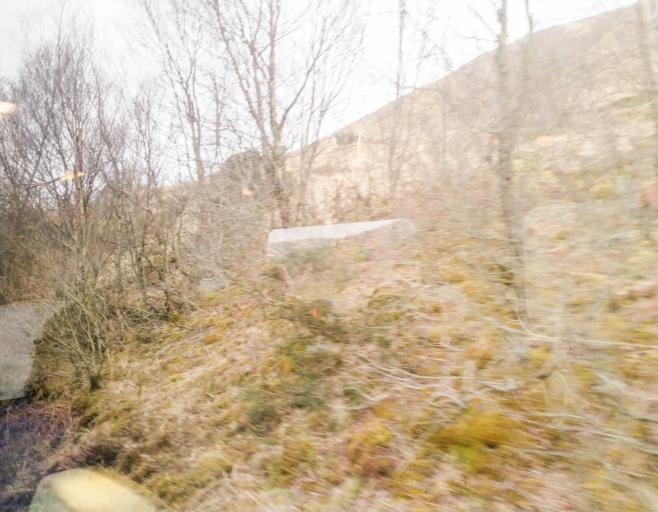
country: GB
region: Scotland
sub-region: Argyll and Bute
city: Garelochhead
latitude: 56.4705
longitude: -4.7174
